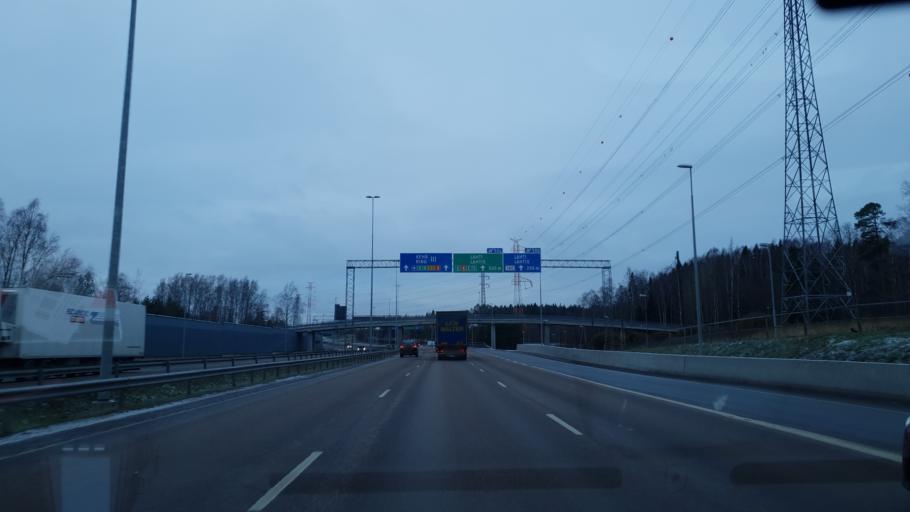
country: FI
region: Uusimaa
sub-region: Helsinki
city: Vantaa
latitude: 60.2703
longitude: 25.1000
